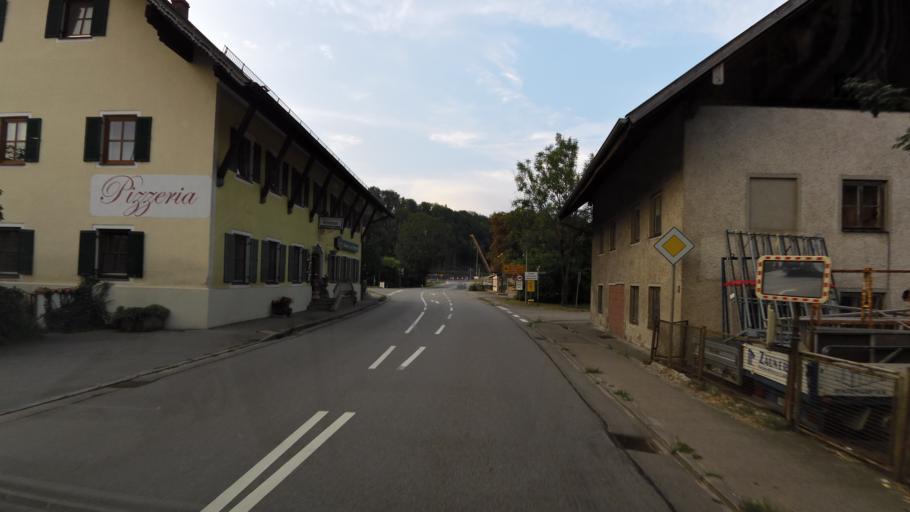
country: DE
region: Bavaria
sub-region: Lower Bavaria
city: Kirchham
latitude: 48.3501
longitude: 13.2493
